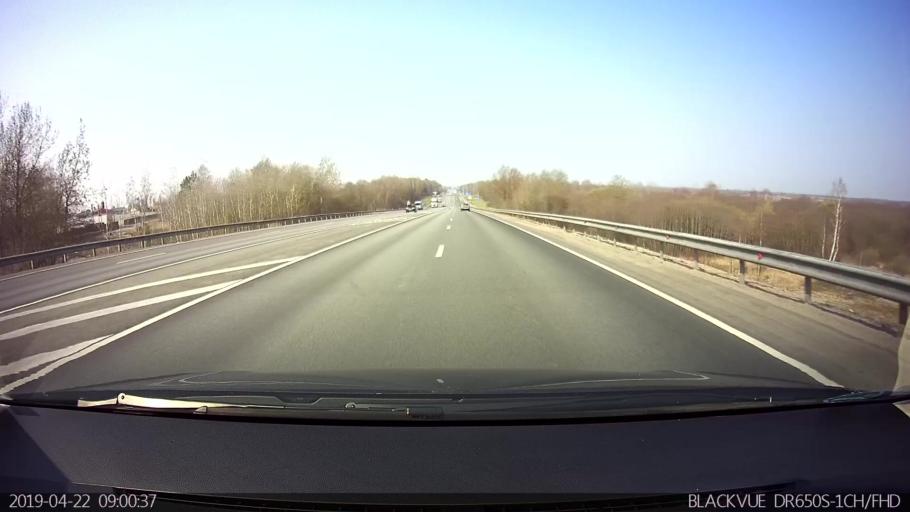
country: RU
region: Smolensk
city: Pechersk
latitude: 54.8622
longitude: 31.9393
